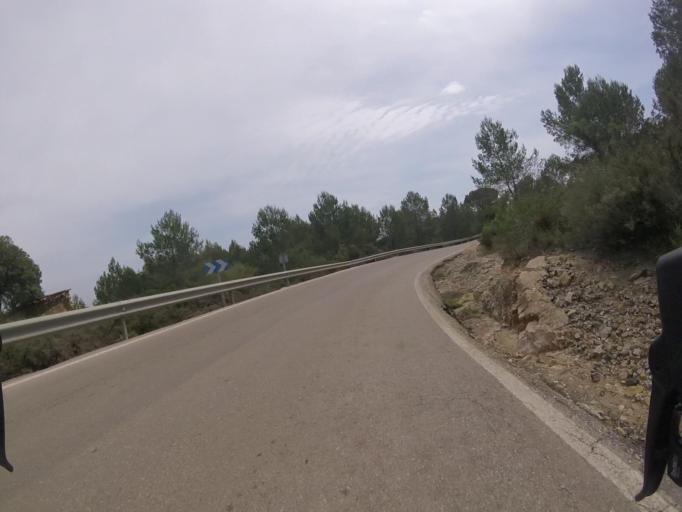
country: ES
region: Valencia
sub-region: Provincia de Castello
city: Cabanes
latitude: 40.1589
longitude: 0.0829
